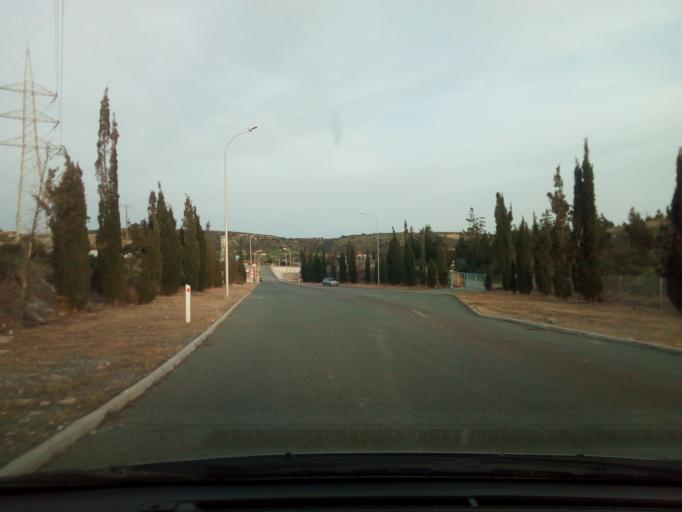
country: CY
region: Limassol
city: Pyrgos
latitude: 34.7315
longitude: 33.2859
